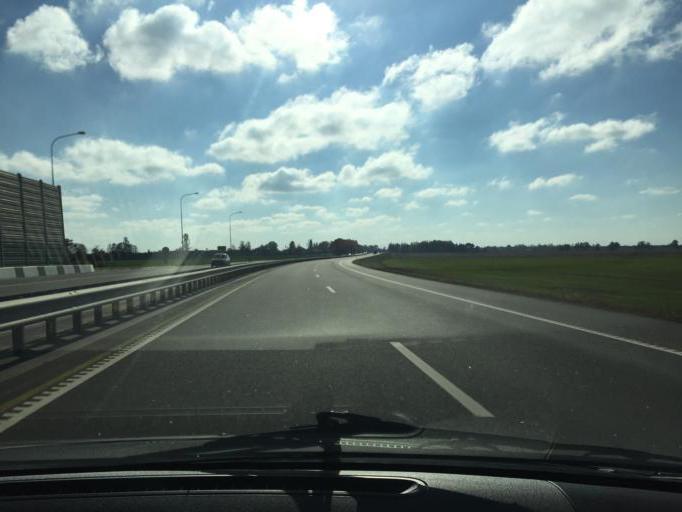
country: BY
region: Minsk
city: Slutsk
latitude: 53.0992
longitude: 27.5712
